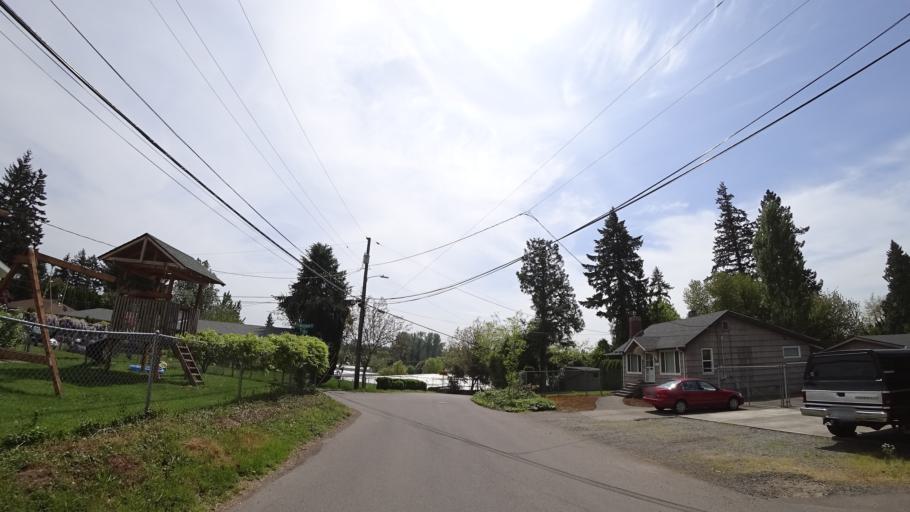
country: US
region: Oregon
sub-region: Clackamas County
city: Milwaukie
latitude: 45.4597
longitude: -122.6067
